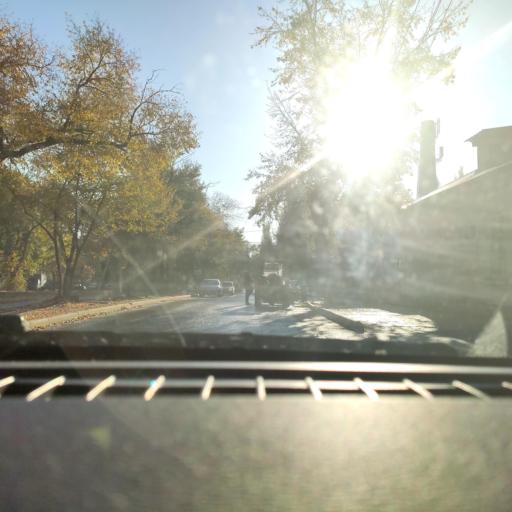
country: RU
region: Voronezj
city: Maslovka
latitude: 51.6148
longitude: 39.2482
